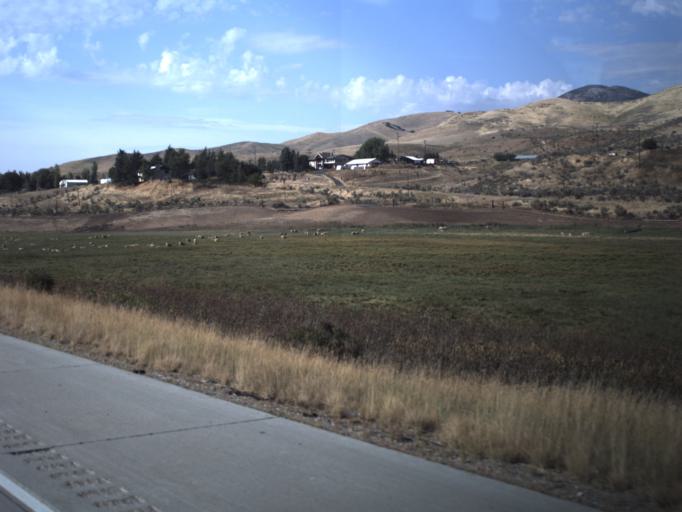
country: US
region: Utah
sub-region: Morgan County
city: Morgan
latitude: 41.0754
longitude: -111.7207
